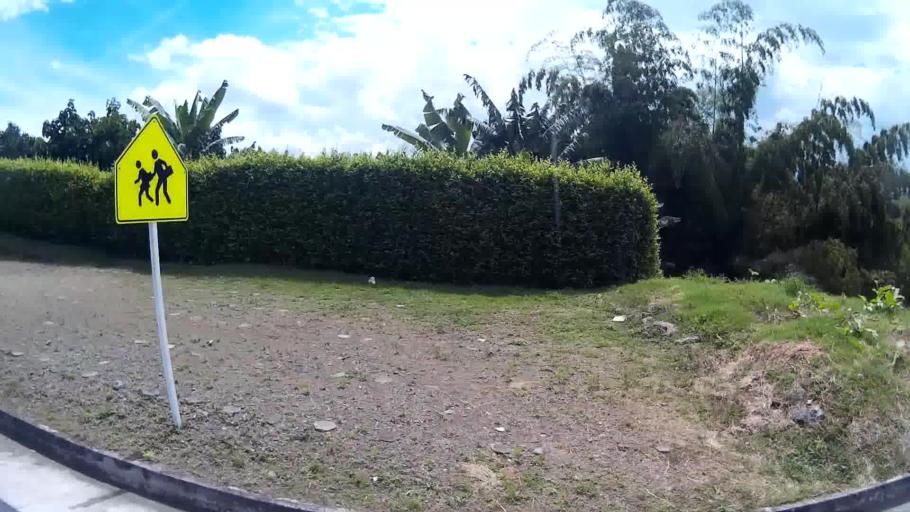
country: CO
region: Risaralda
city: Pereira
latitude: 4.7818
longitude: -75.7230
